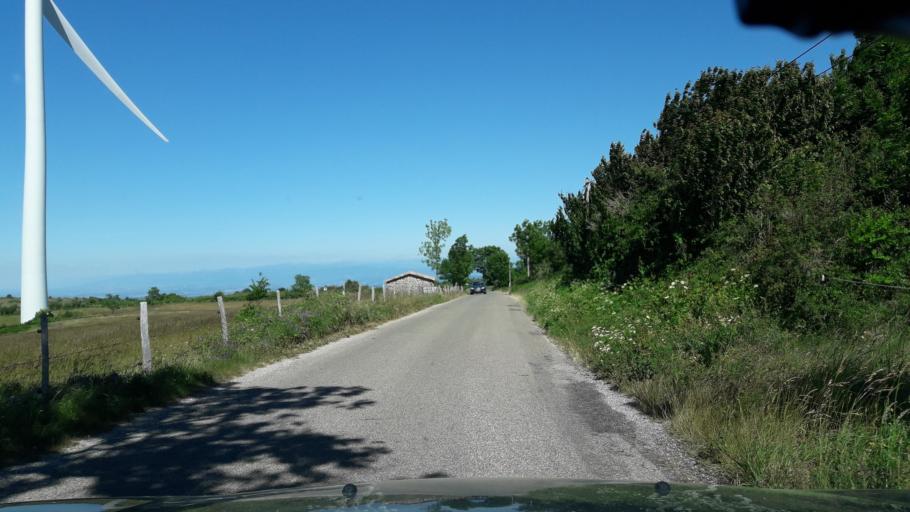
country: FR
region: Rhone-Alpes
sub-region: Departement de l'Ardeche
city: Saint-Priest
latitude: 44.6873
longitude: 4.5694
